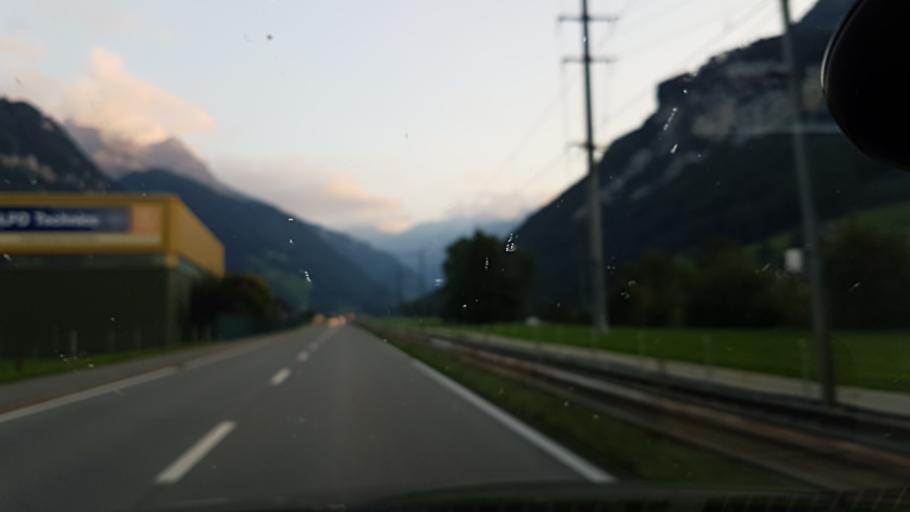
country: CH
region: Nidwalden
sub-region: Nidwalden
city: Dallenwil
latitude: 46.9247
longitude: 8.3978
